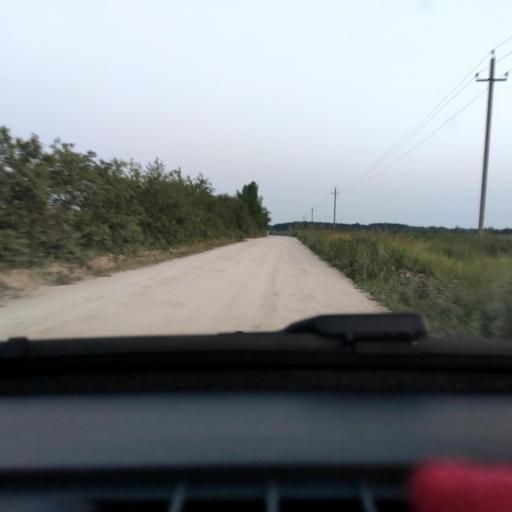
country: RU
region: Voronezj
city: Podgornoye
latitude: 51.8624
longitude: 39.1035
